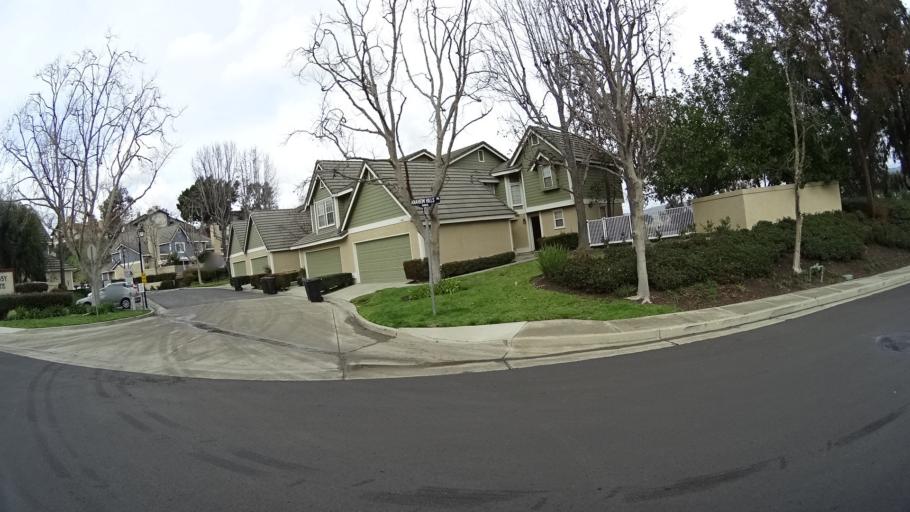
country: US
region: California
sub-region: Orange County
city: Villa Park
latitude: 33.8409
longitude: -117.7780
